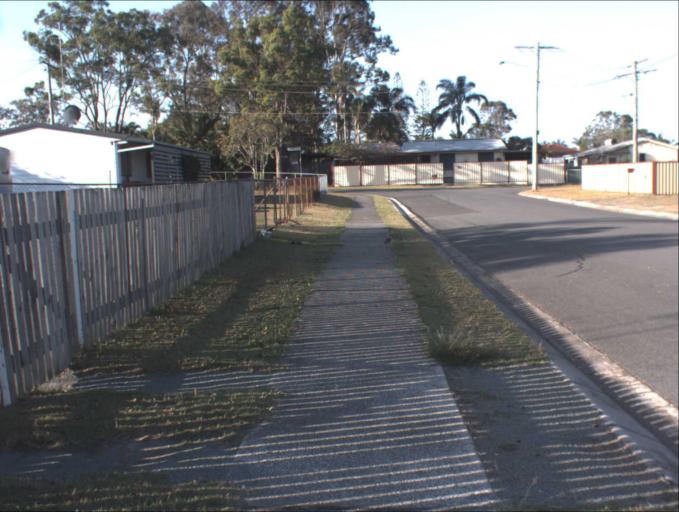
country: AU
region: Queensland
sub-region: Gold Coast
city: Yatala
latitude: -27.7078
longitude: 153.2158
